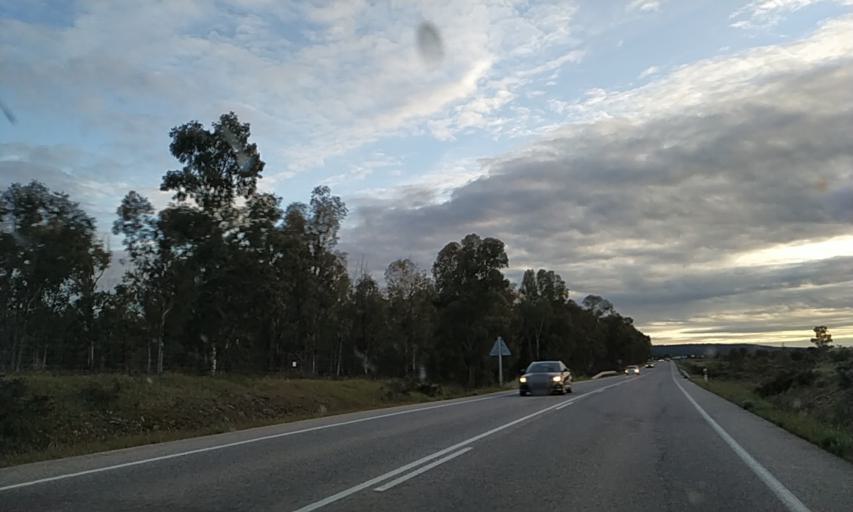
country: ES
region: Extremadura
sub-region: Provincia de Caceres
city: Malpartida de Caceres
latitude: 39.3295
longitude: -6.4891
